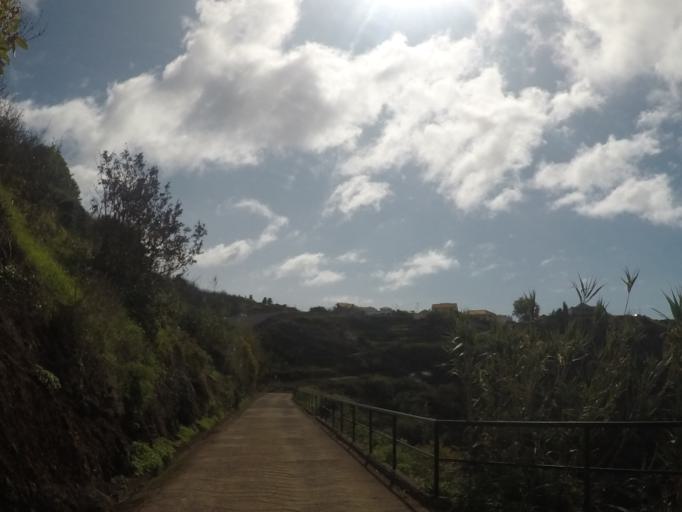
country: PT
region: Madeira
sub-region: Calheta
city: Faja da Ovelha
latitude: 32.8166
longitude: -17.2438
